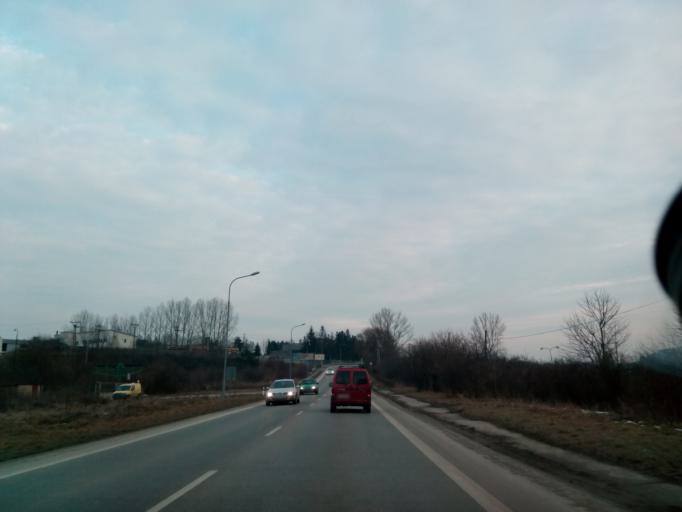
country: SK
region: Presovsky
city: Sabinov
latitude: 49.1138
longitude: 21.0766
